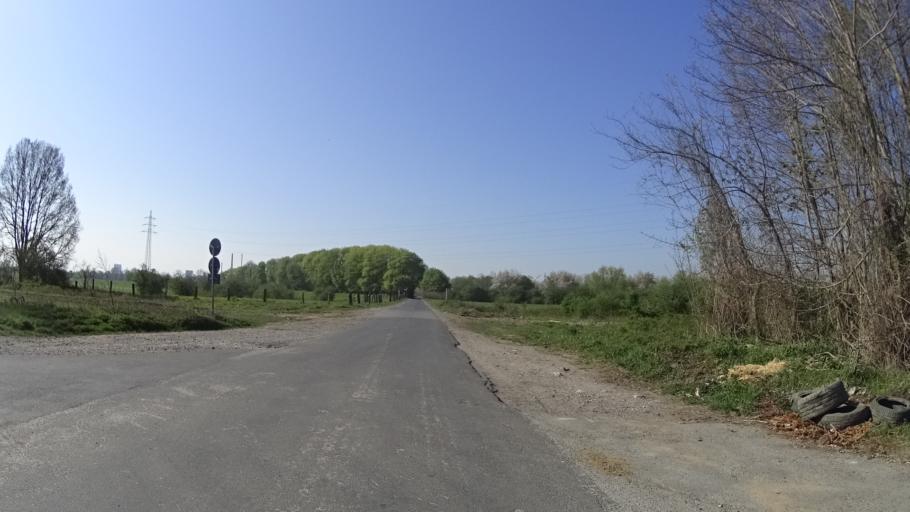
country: DE
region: North Rhine-Westphalia
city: Rheinberg
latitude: 51.5820
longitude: 6.5791
